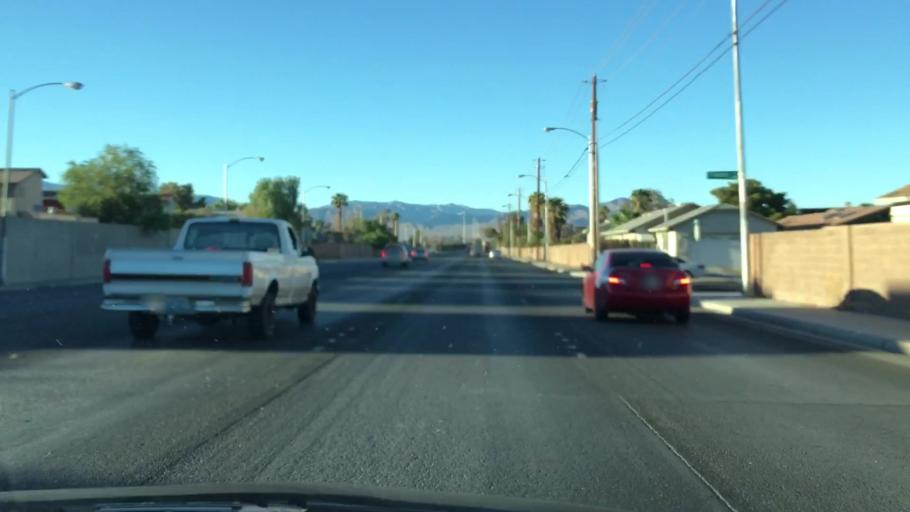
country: US
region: Nevada
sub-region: Clark County
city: Sunrise Manor
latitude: 36.2290
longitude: -115.0801
